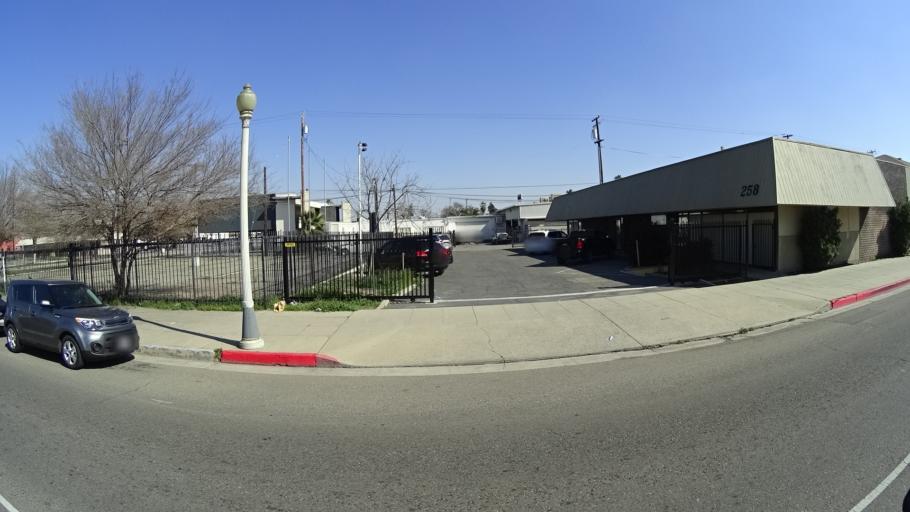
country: US
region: California
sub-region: Fresno County
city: Fresno
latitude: 36.7465
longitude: -119.7906
